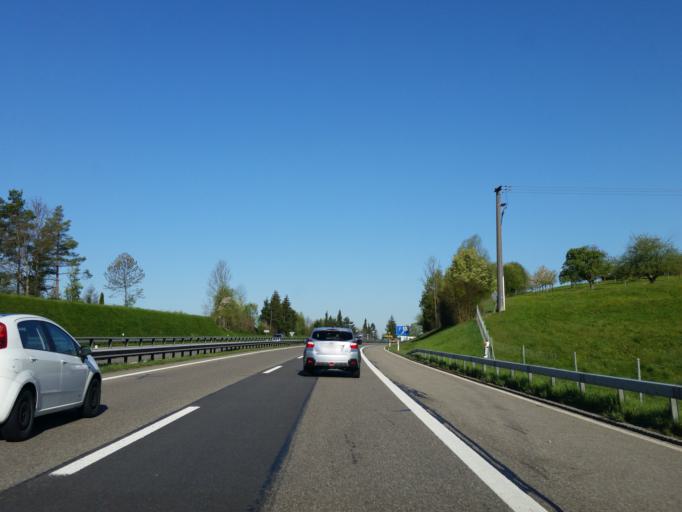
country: CH
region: Saint Gallen
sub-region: Wahlkreis St. Gallen
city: Gossau
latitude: 47.4208
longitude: 9.2666
